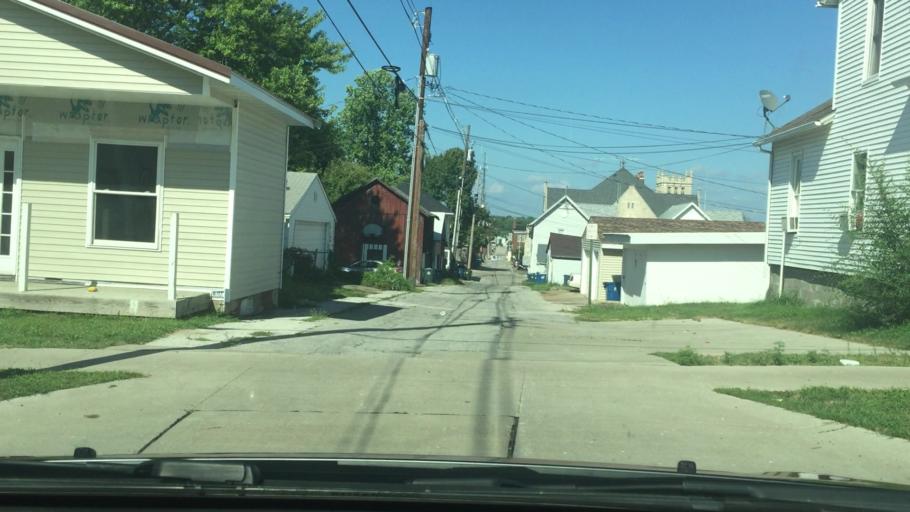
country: US
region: Iowa
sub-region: Muscatine County
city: Muscatine
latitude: 41.4220
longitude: -91.0499
